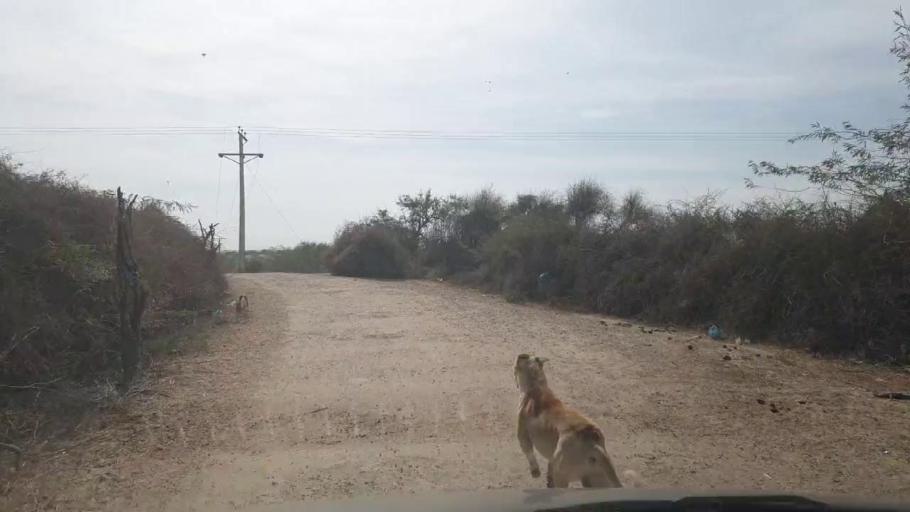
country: PK
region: Sindh
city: Umarkot
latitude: 25.2981
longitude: 69.7424
